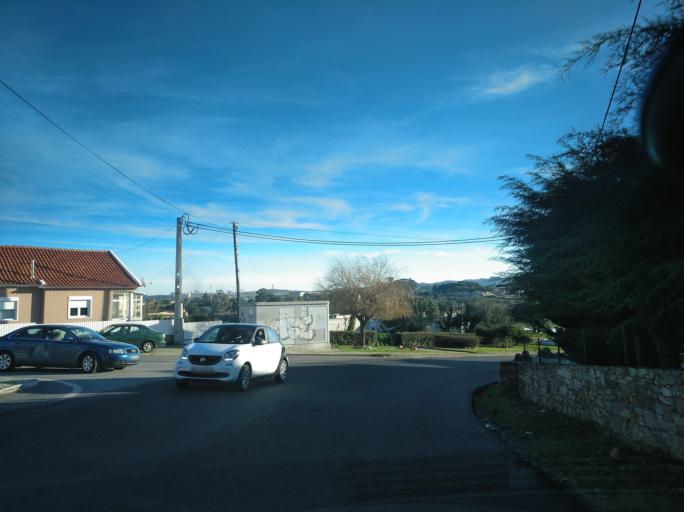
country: PT
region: Lisbon
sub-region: Sintra
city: Sintra
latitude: 38.8324
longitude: -9.3698
